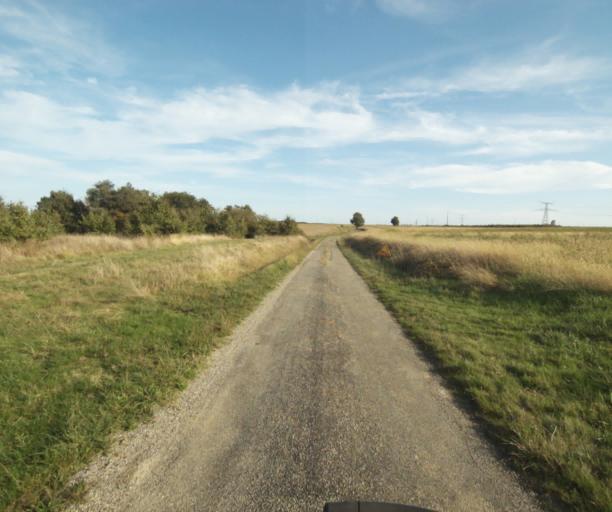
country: FR
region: Midi-Pyrenees
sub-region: Departement du Tarn-et-Garonne
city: Finhan
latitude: 43.9110
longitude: 1.1088
